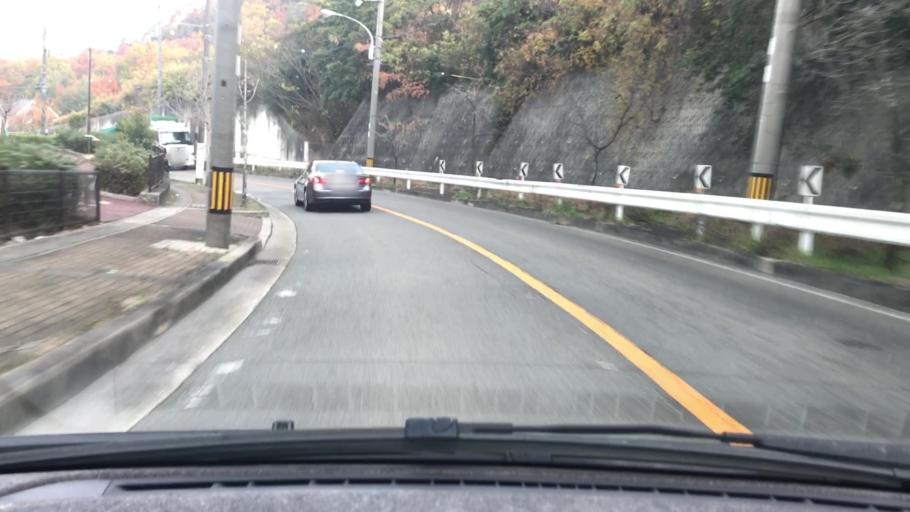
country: JP
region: Hyogo
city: Sandacho
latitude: 34.8246
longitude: 135.2519
